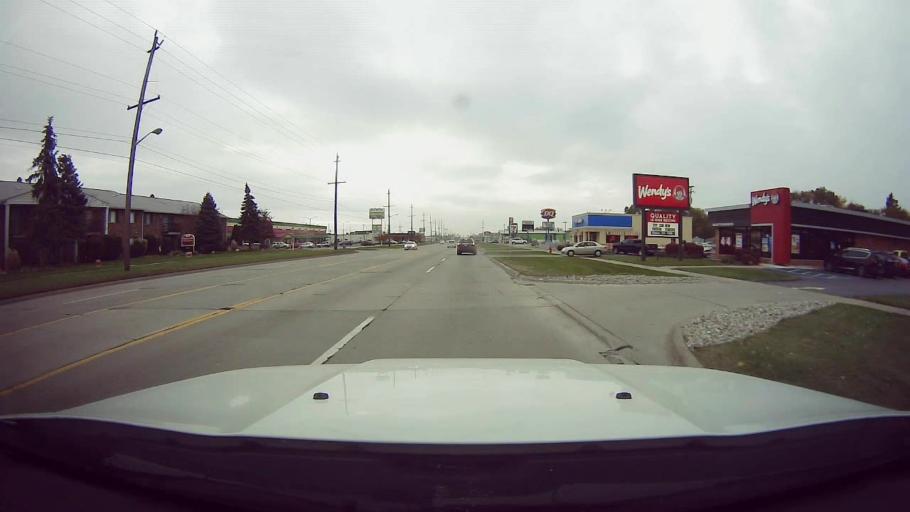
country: US
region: Michigan
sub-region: Oakland County
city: Madison Heights
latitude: 42.5086
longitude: -83.0861
